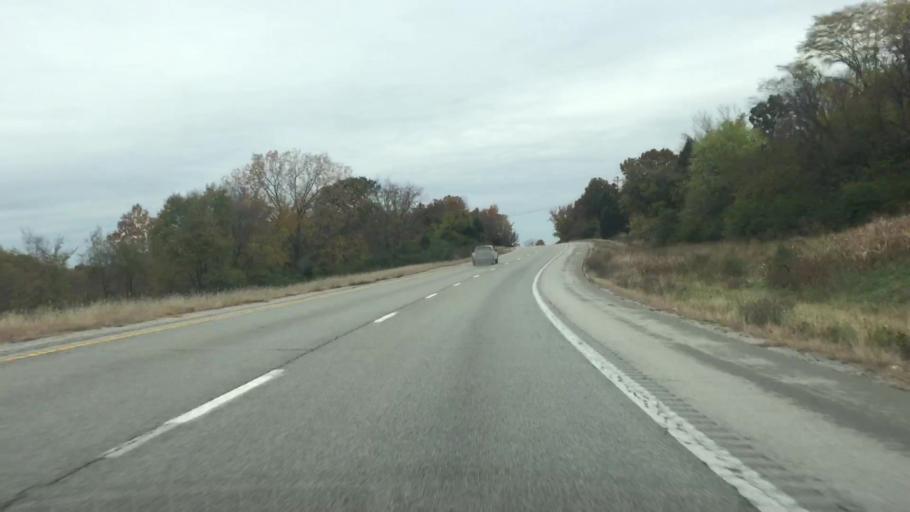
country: US
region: Missouri
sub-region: Jackson County
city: Lees Summit
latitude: 38.9522
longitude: -94.4159
